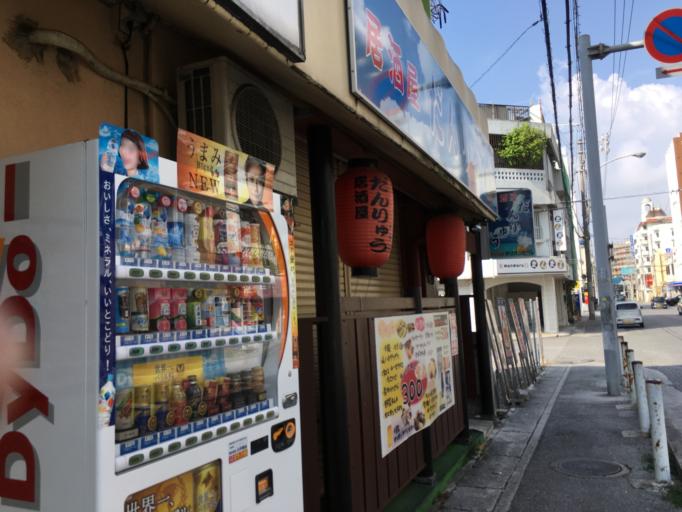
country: JP
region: Okinawa
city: Naha-shi
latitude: 26.2225
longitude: 127.6798
